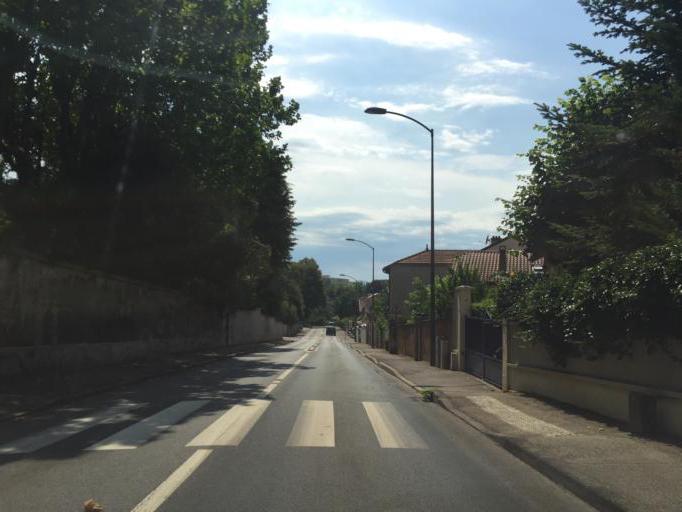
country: FR
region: Rhone-Alpes
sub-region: Departement du Rhone
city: Ecully
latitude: 45.7705
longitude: 4.7722
